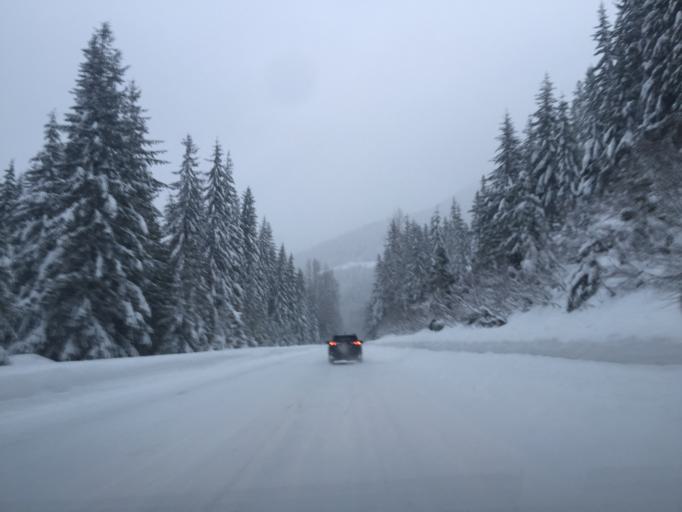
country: US
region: Washington
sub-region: Chelan County
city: Leavenworth
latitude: 47.7758
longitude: -121.0204
